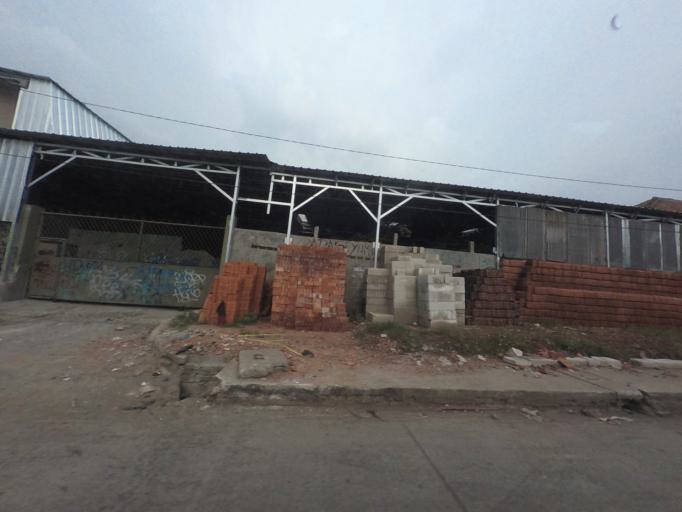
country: ID
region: West Java
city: Cicurug
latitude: -6.7607
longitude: 106.8002
